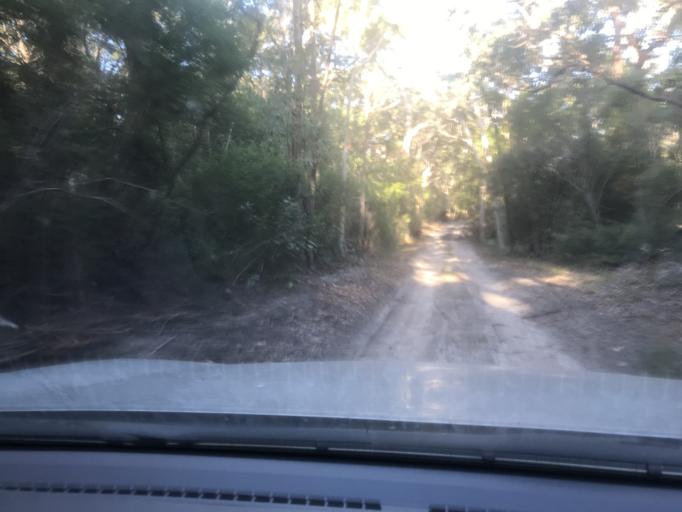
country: AU
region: Queensland
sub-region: Fraser Coast
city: Urangan
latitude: -25.3710
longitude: 153.1636
